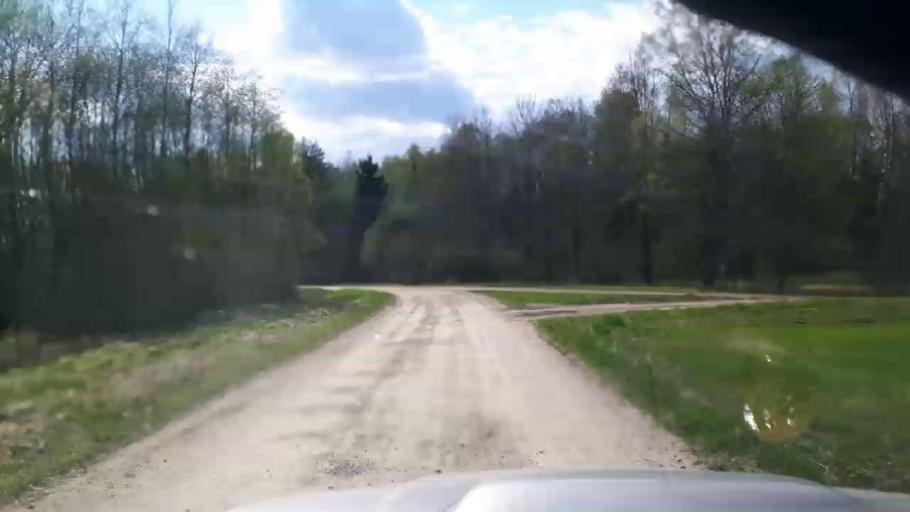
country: EE
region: Paernumaa
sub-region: Sindi linn
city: Sindi
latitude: 58.4291
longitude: 24.7689
